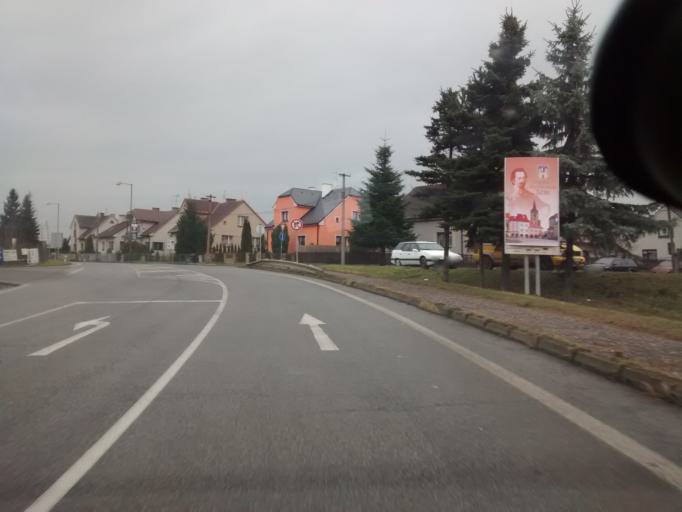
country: CZ
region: Kralovehradecky
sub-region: Okres Jicin
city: Jicin
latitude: 50.4256
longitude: 15.3495
